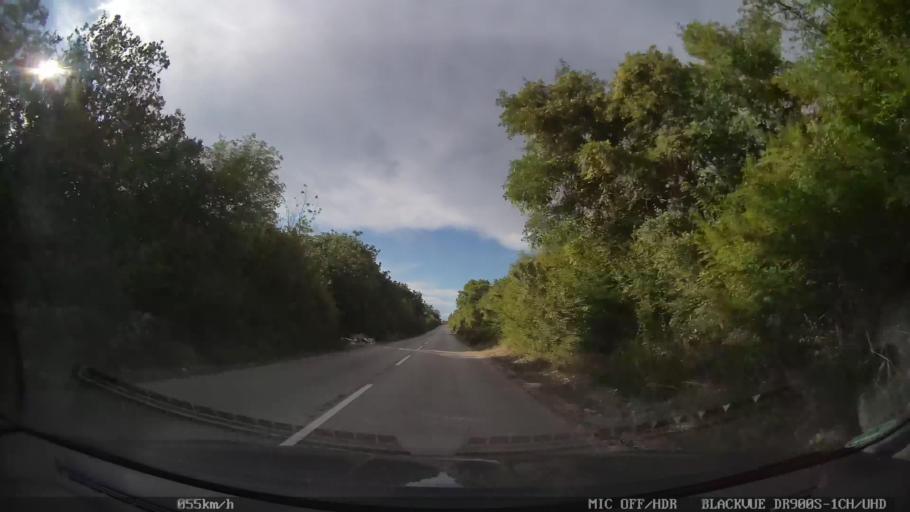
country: HR
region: Primorsko-Goranska
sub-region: Grad Krk
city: Krk
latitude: 45.0647
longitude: 14.4744
